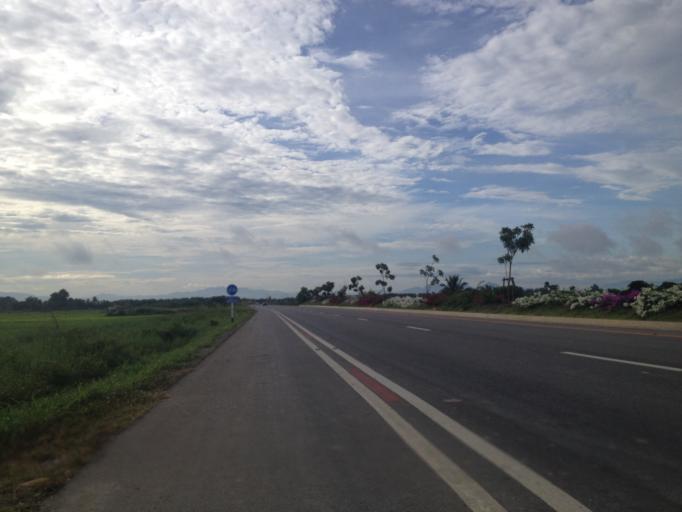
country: TH
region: Chiang Mai
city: San Pa Tong
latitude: 18.5771
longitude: 98.8446
